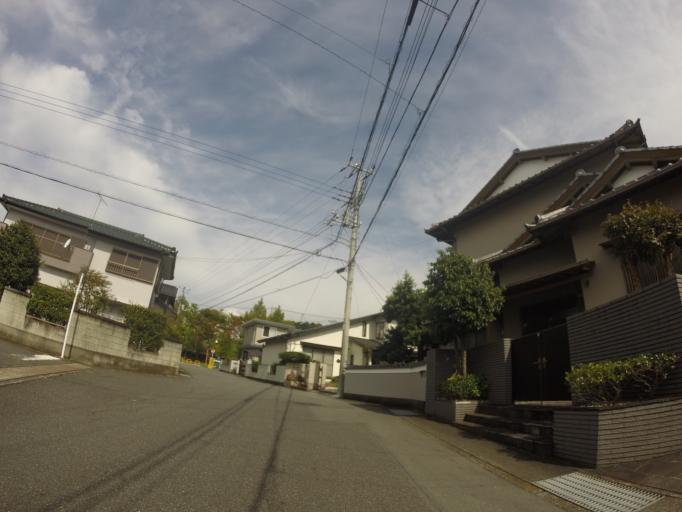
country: JP
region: Shizuoka
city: Fuji
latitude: 35.1936
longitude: 138.6968
